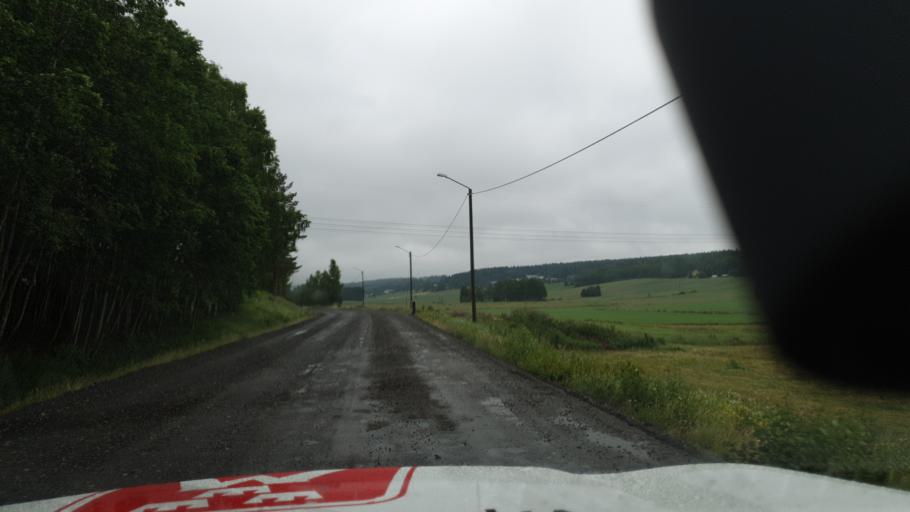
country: SE
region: Vaesterbotten
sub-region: Vannas Kommun
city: Vaennaes
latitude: 63.7422
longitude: 19.6511
